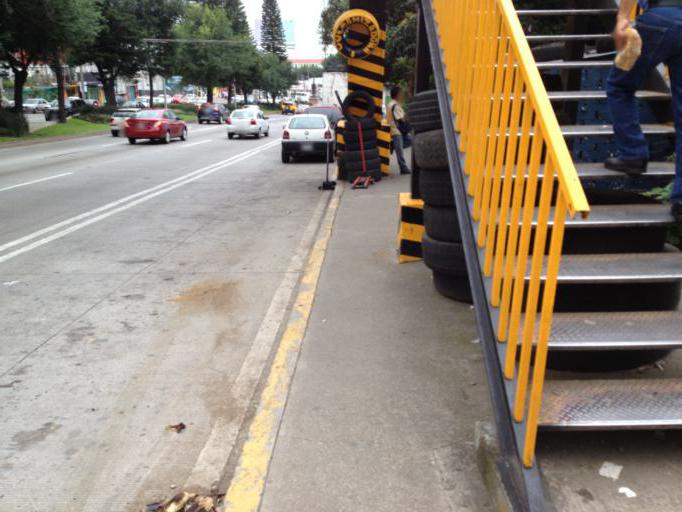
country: MX
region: Veracruz
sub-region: Xalapa
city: Xalapa de Enriquez
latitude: 19.5295
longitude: -96.9005
